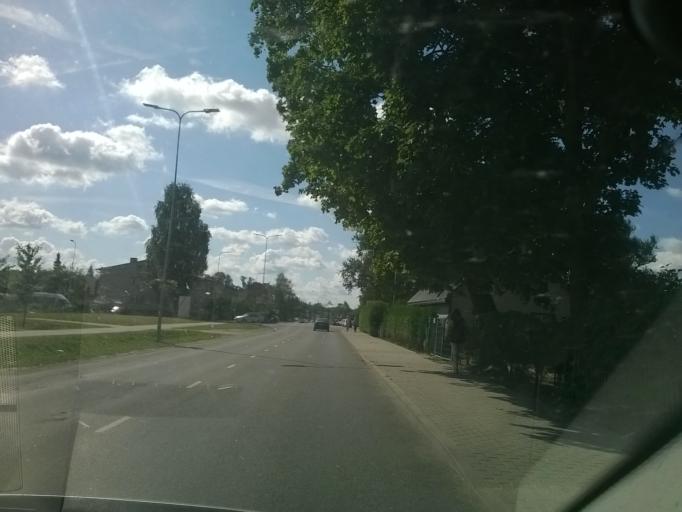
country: EE
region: Vorumaa
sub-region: Voru linn
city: Voru
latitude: 57.8397
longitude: 27.0073
